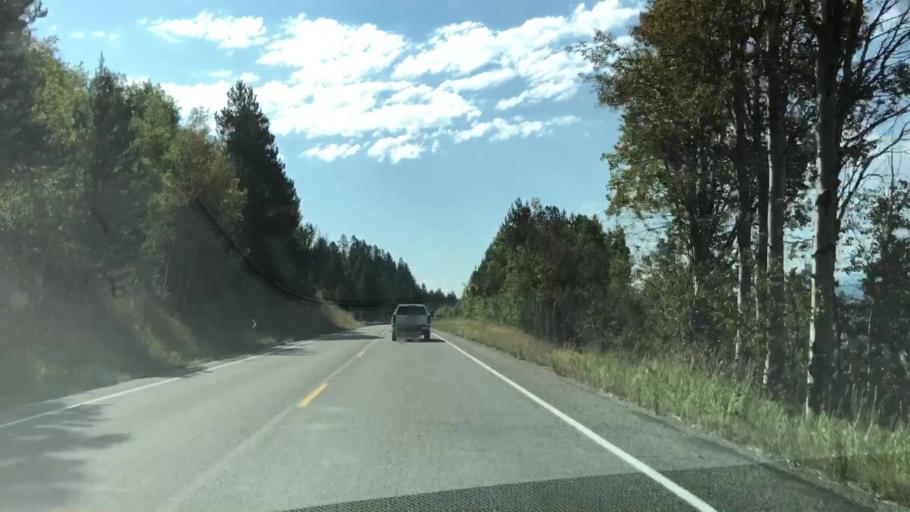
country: US
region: Idaho
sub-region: Teton County
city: Victor
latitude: 43.2910
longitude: -111.1236
